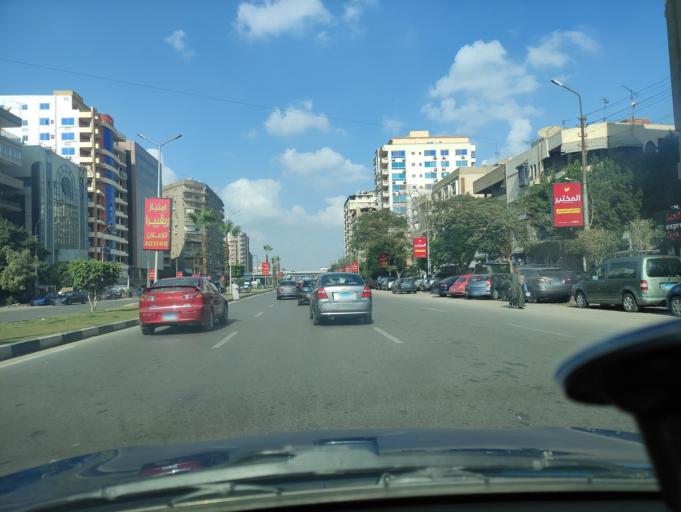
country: EG
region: Muhafazat al Qahirah
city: Cairo
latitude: 30.0880
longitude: 31.3413
